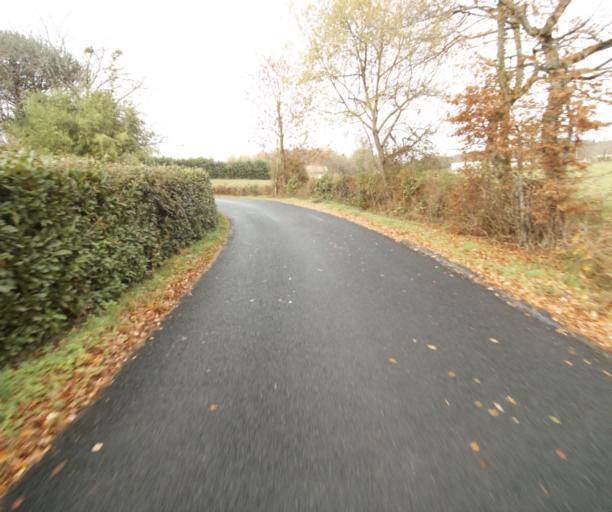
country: FR
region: Limousin
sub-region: Departement de la Correze
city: Saint-Mexant
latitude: 45.2684
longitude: 1.6351
